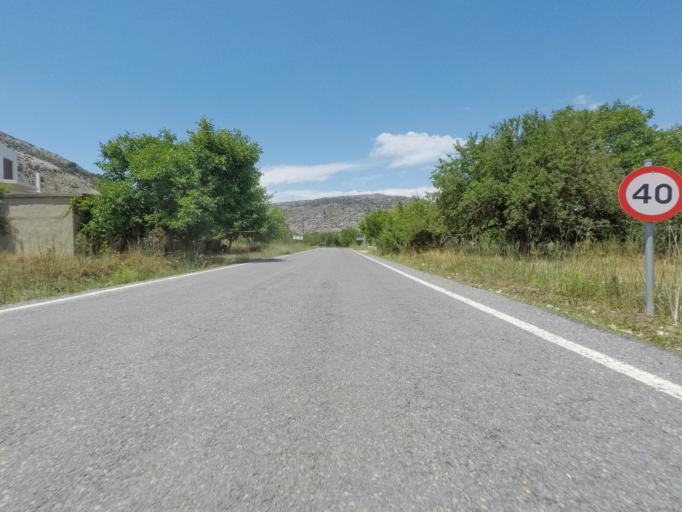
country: GR
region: Crete
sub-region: Nomos Irakleiou
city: Mokhos
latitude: 35.1827
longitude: 25.4331
